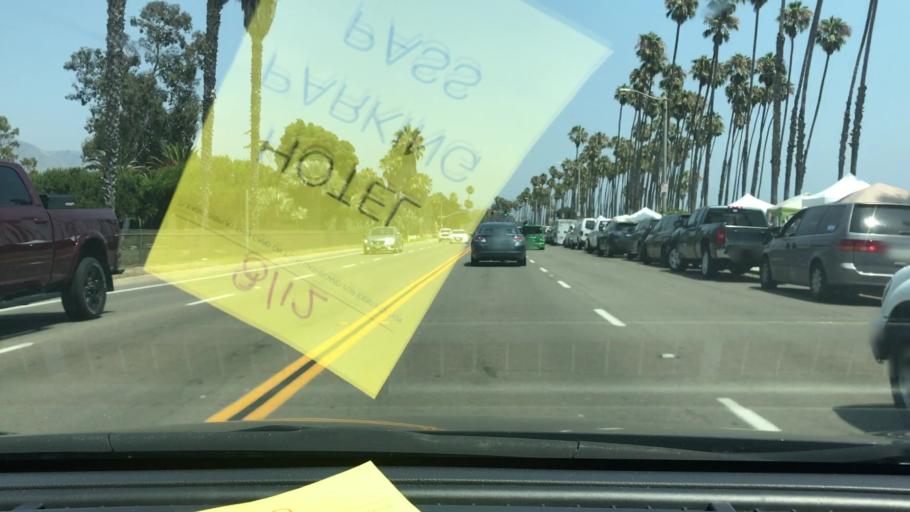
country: US
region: California
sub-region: Santa Barbara County
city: Santa Barbara
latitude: 34.4151
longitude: -119.6829
